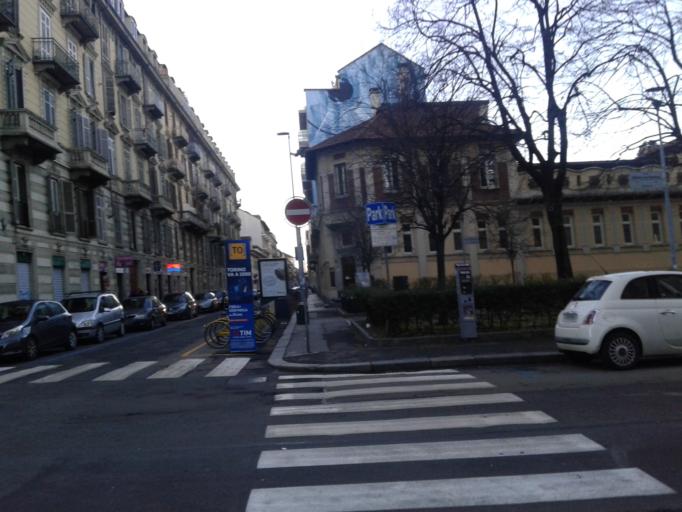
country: IT
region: Piedmont
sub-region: Provincia di Torino
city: Turin
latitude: 45.0544
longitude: 7.6785
